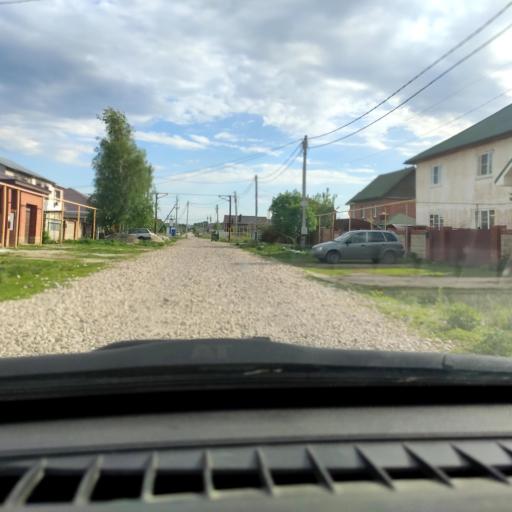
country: RU
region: Samara
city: Tol'yatti
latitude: 53.5670
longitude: 49.4080
